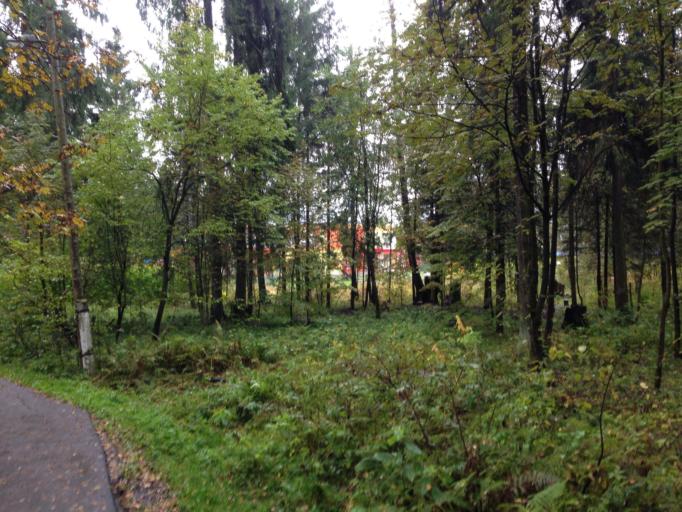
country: RU
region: Moskovskaya
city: Zelenogradskiy
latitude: 56.0947
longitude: 37.9049
